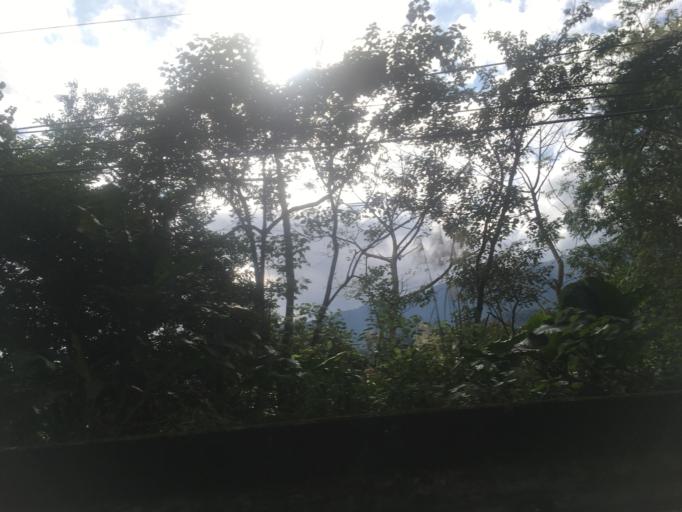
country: TW
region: Taiwan
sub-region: Yilan
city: Yilan
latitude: 24.6469
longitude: 121.5662
